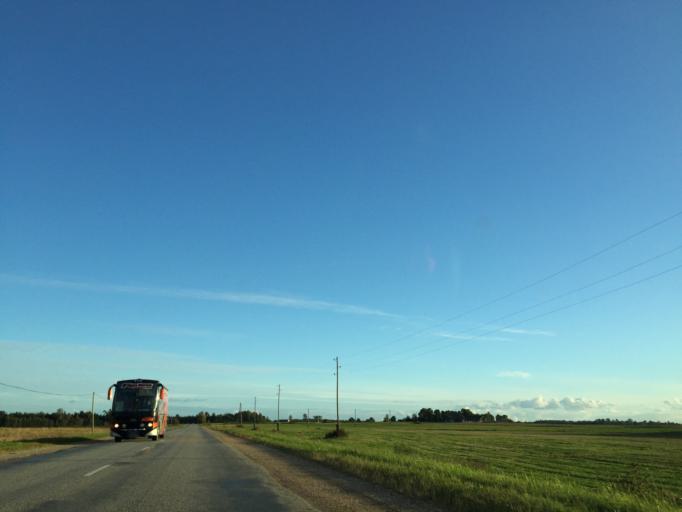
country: LV
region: Saldus Rajons
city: Saldus
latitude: 56.7413
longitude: 22.3774
